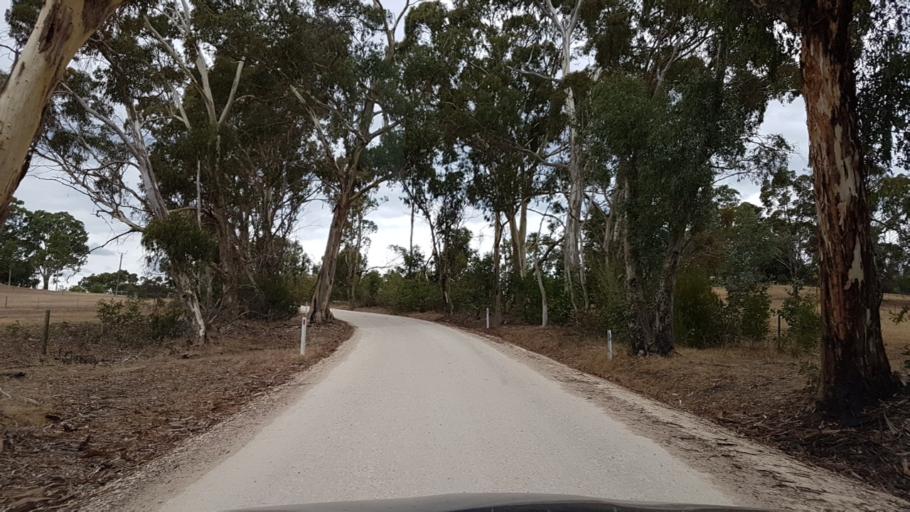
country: AU
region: South Australia
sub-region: Adelaide Hills
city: Gumeracha
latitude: -34.7810
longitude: 138.8381
